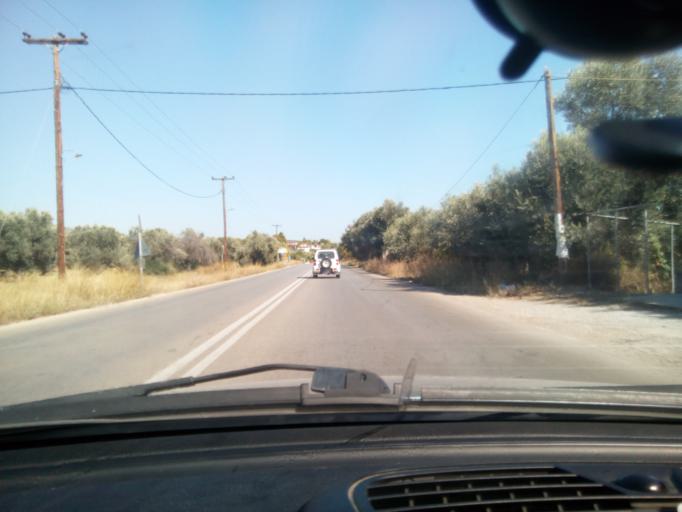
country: GR
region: Central Greece
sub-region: Nomos Evvoias
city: Malakonta
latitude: 38.4108
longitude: 23.7213
